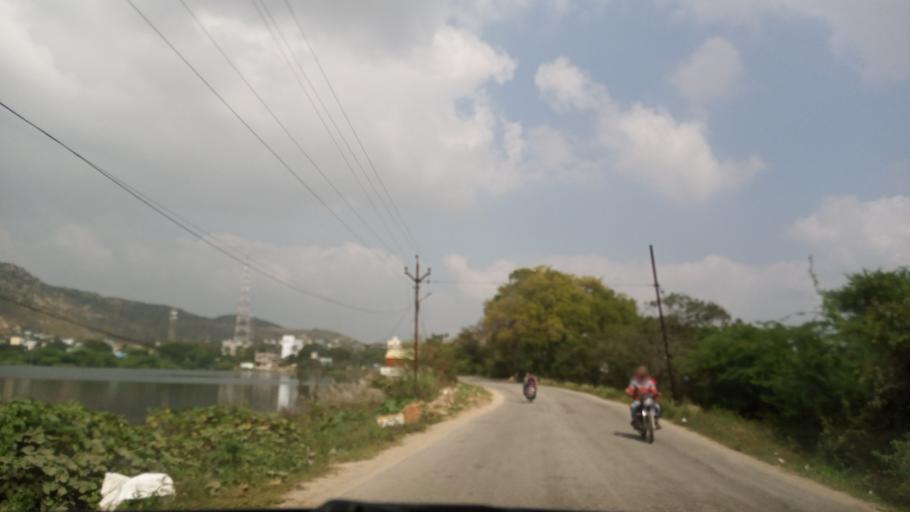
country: IN
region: Andhra Pradesh
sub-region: Chittoor
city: Madanapalle
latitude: 13.5748
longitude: 78.5184
